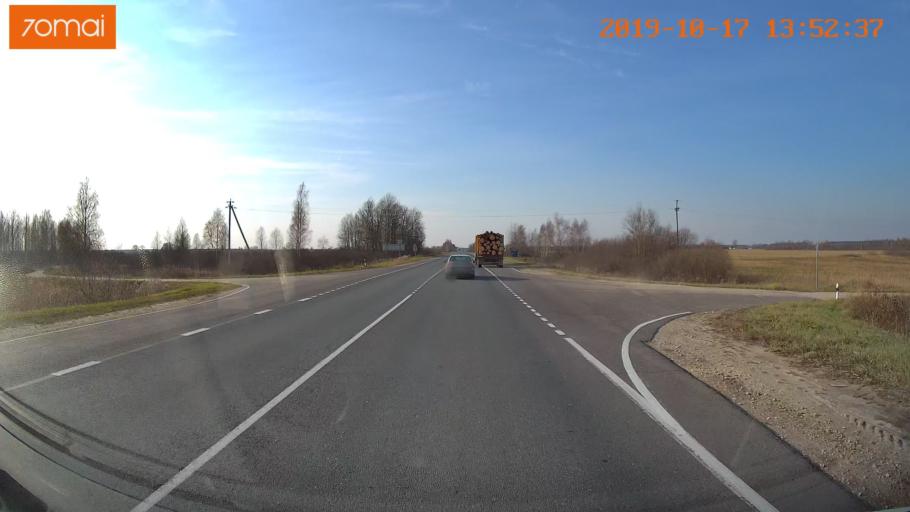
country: RU
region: Rjazan
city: Spas-Klepiki
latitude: 55.1404
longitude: 40.3603
